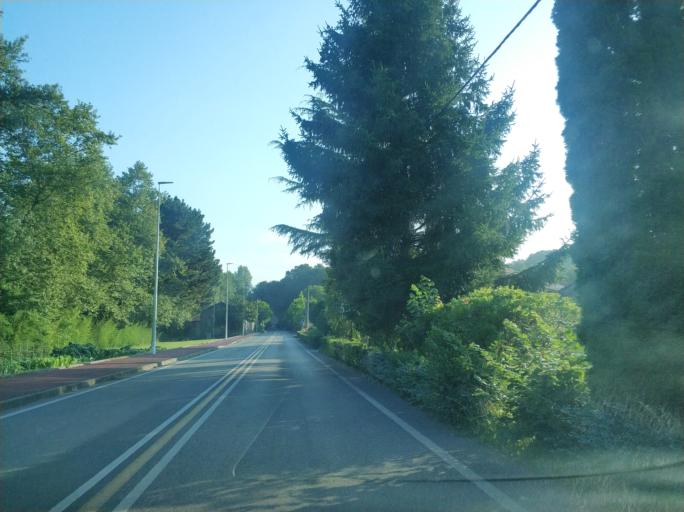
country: ES
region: Cantabria
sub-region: Provincia de Cantabria
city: Miengo
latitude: 43.3936
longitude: -3.9469
